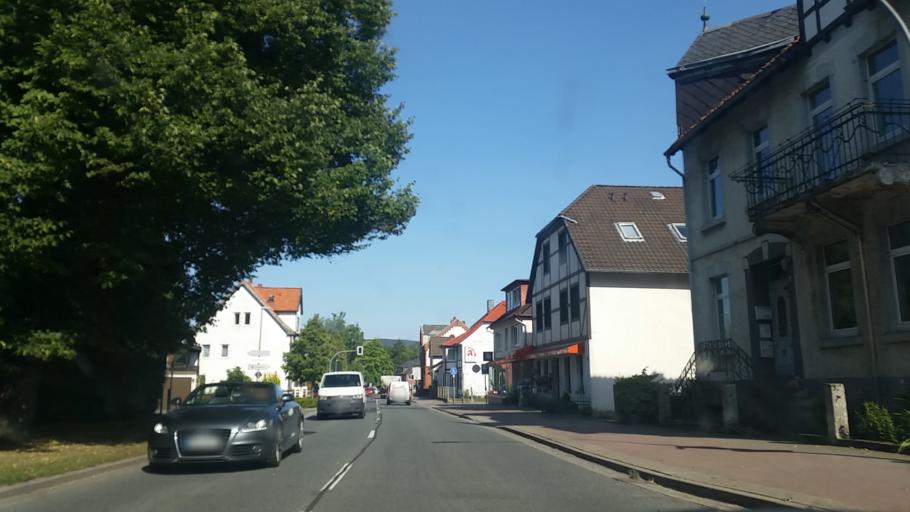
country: DE
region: Lower Saxony
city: Coppenbrugge
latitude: 52.1179
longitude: 9.5413
